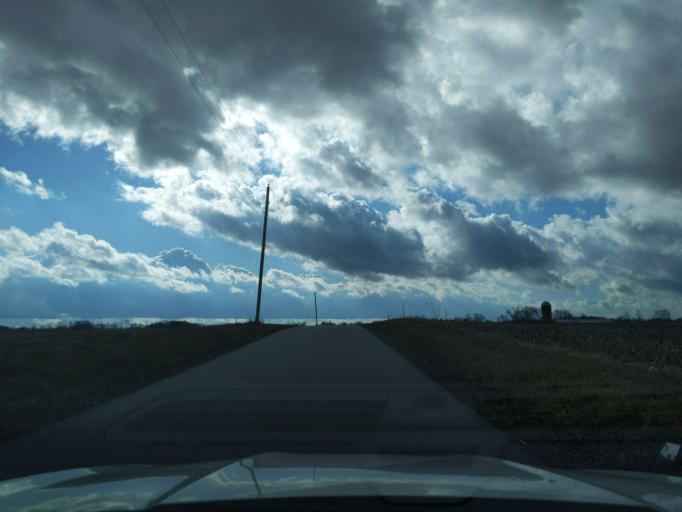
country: US
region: Indiana
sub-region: Decatur County
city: Greensburg
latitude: 39.4034
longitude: -85.5079
